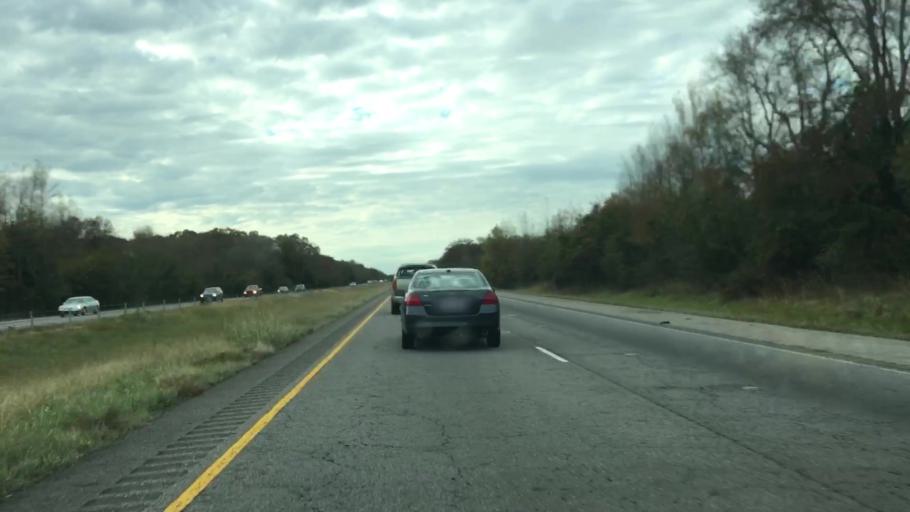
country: US
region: Arkansas
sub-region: Conway County
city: Morrilton
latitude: 35.1611
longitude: -92.5994
